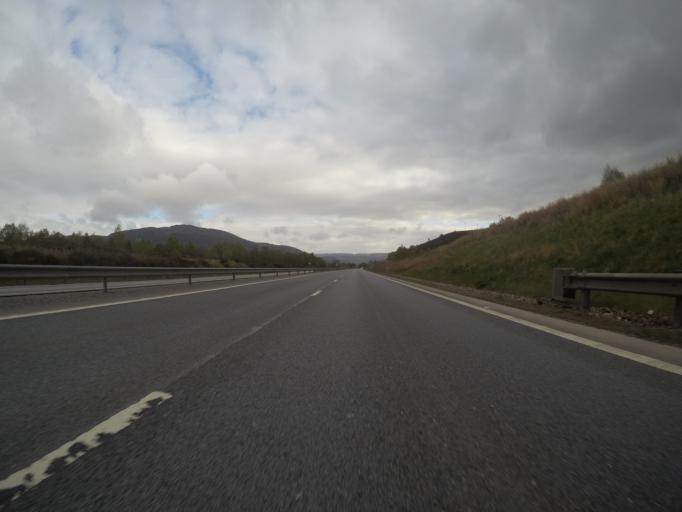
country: GB
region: Scotland
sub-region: Highland
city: Kingussie
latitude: 57.0192
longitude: -4.1604
